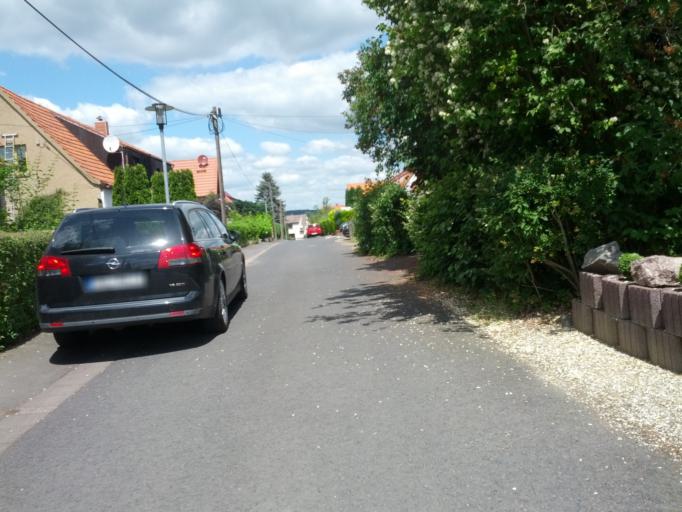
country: DE
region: Thuringia
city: Bischofroda
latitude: 51.0037
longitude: 10.3601
